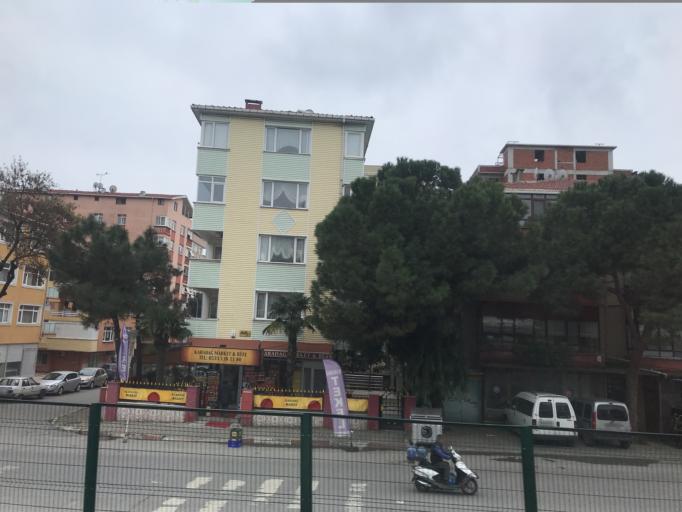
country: TR
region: Istanbul
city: Maltepe
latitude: 40.9057
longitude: 29.1610
